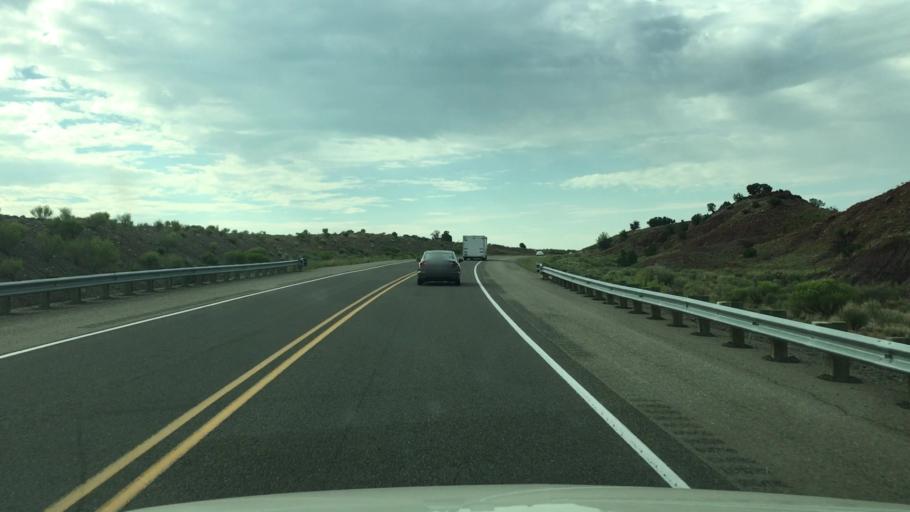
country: US
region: New Mexico
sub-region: Santa Fe County
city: Eldorado at Santa Fe
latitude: 35.2715
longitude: -105.8107
